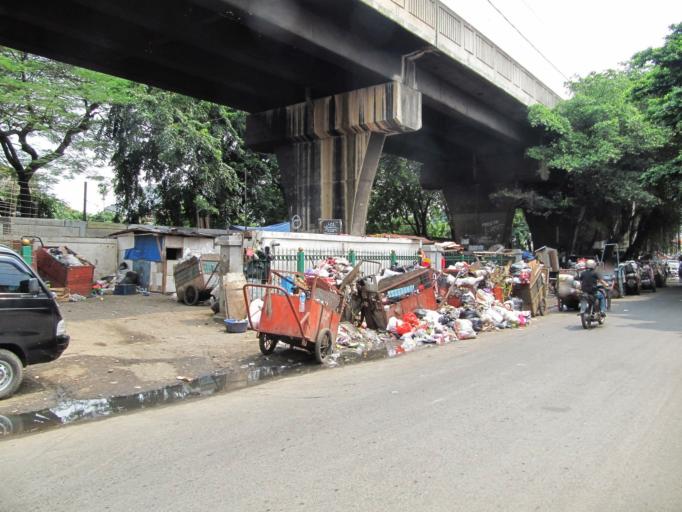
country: ID
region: Jakarta Raya
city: Jakarta
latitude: -6.1479
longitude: 106.8267
